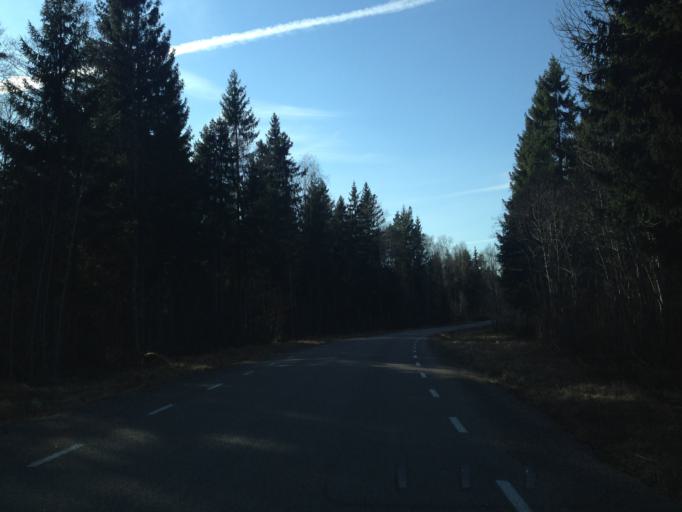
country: EE
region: Harju
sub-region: Nissi vald
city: Turba
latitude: 59.1452
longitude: 24.1545
